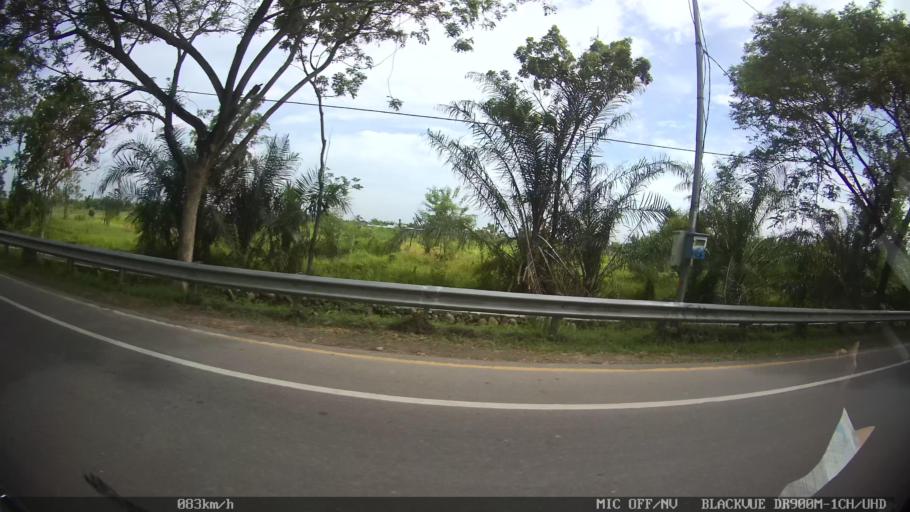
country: ID
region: North Sumatra
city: Percut
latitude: 3.5993
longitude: 98.8225
